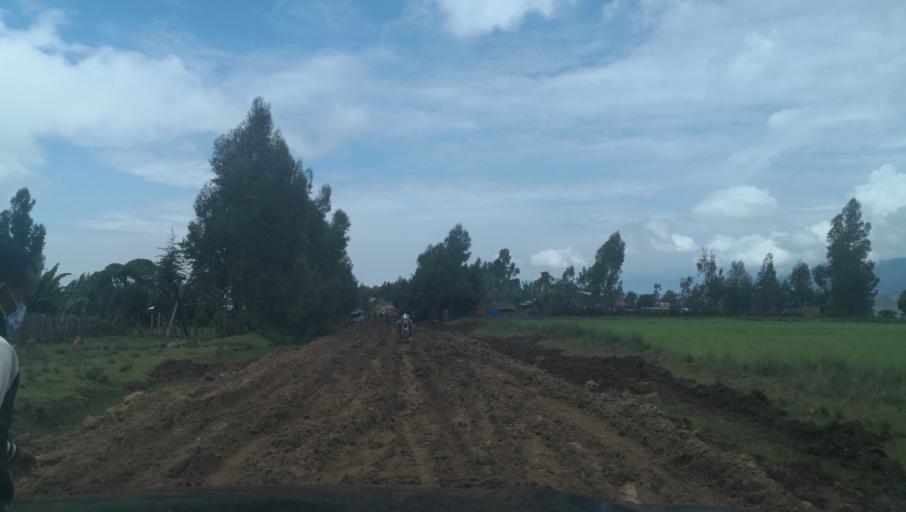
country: ET
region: Southern Nations, Nationalities, and People's Region
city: Butajira
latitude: 8.2903
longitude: 38.4730
